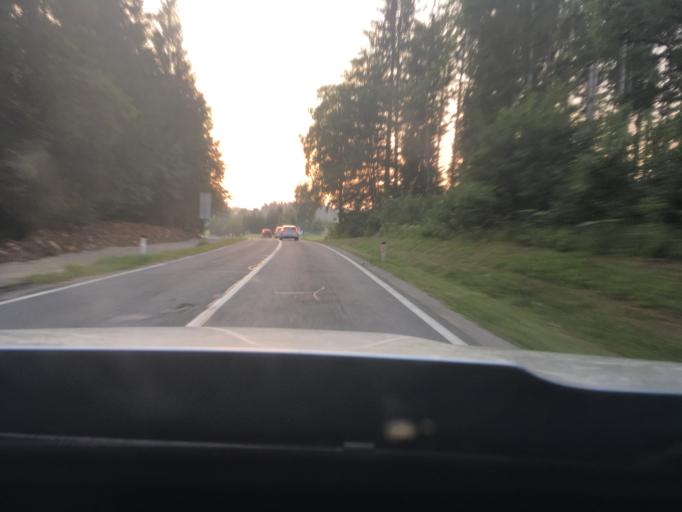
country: SI
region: Kocevje
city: Kocevje
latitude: 45.6831
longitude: 14.8178
